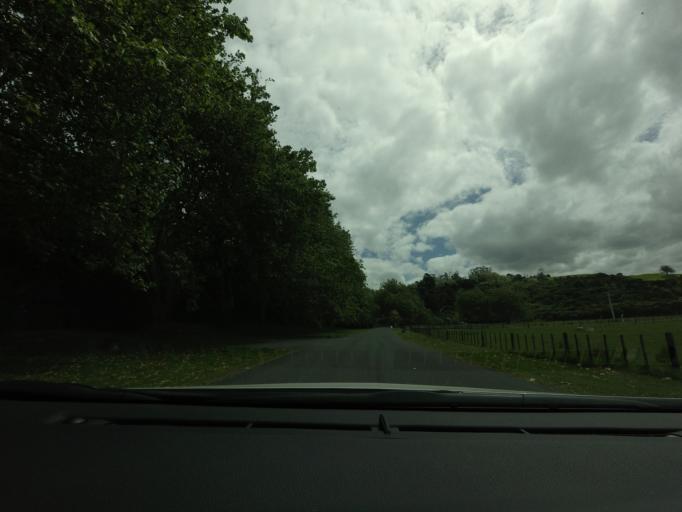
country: NZ
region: Auckland
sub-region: Auckland
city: Warkworth
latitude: -36.5355
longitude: 174.7064
